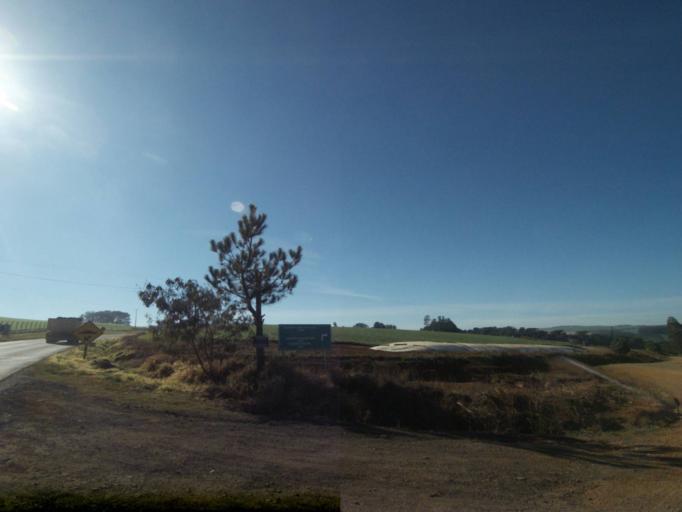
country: BR
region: Parana
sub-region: Tibagi
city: Tibagi
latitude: -24.5262
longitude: -50.3824
